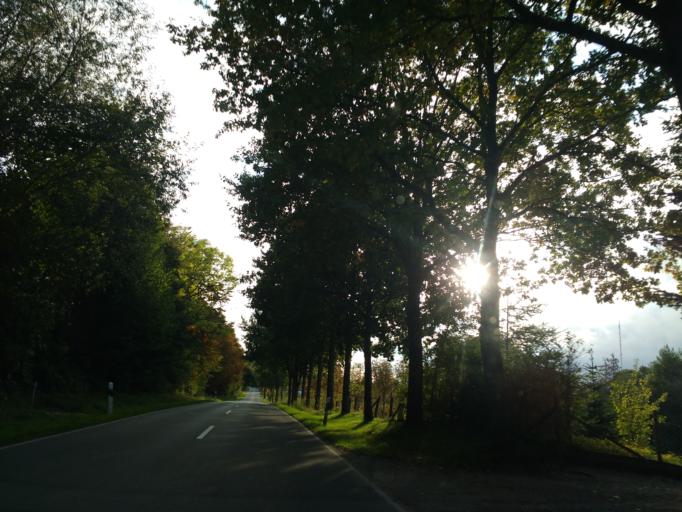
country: DE
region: Schleswig-Holstein
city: Schonwalde am Bungsberg
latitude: 54.2237
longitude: 10.7411
